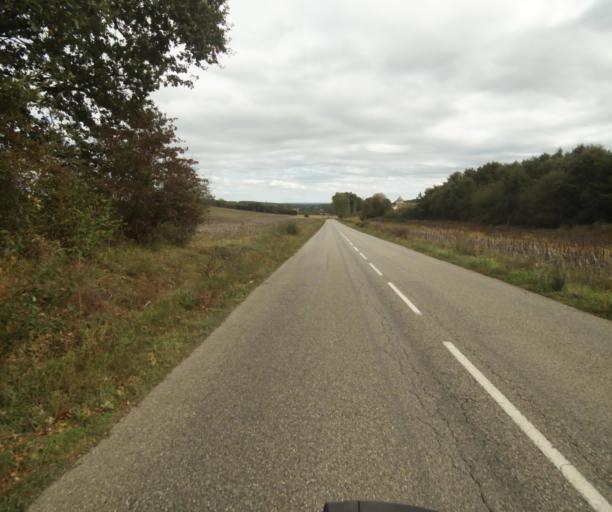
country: FR
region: Midi-Pyrenees
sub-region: Departement du Tarn-et-Garonne
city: Verdun-sur-Garonne
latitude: 43.8578
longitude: 1.1202
